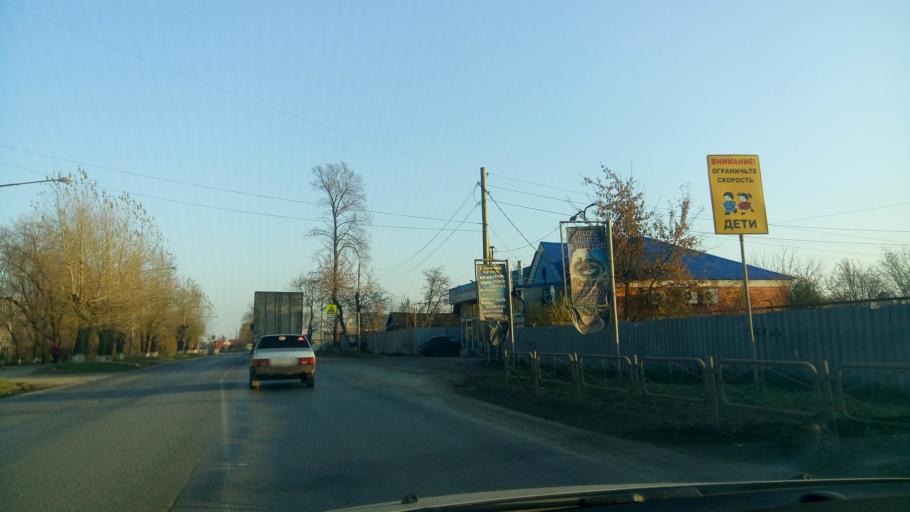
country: RU
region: Sverdlovsk
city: Bogdanovich
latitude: 56.7702
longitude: 62.0459
